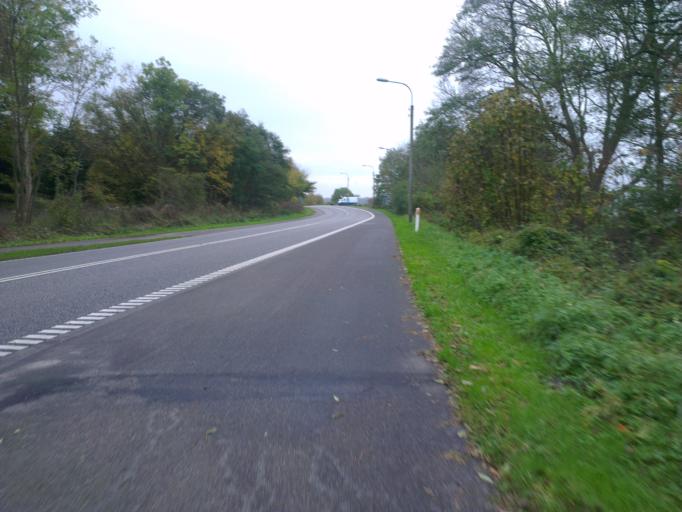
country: DK
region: Capital Region
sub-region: Frederikssund Kommune
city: Jaegerspris
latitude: 55.8545
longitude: 12.0161
